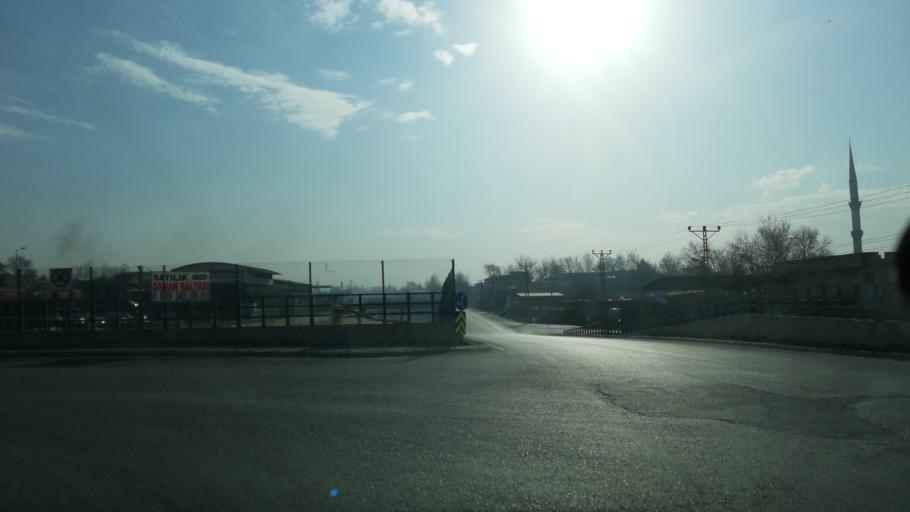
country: TR
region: Kahramanmaras
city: Kahramanmaras
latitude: 37.5620
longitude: 36.9174
